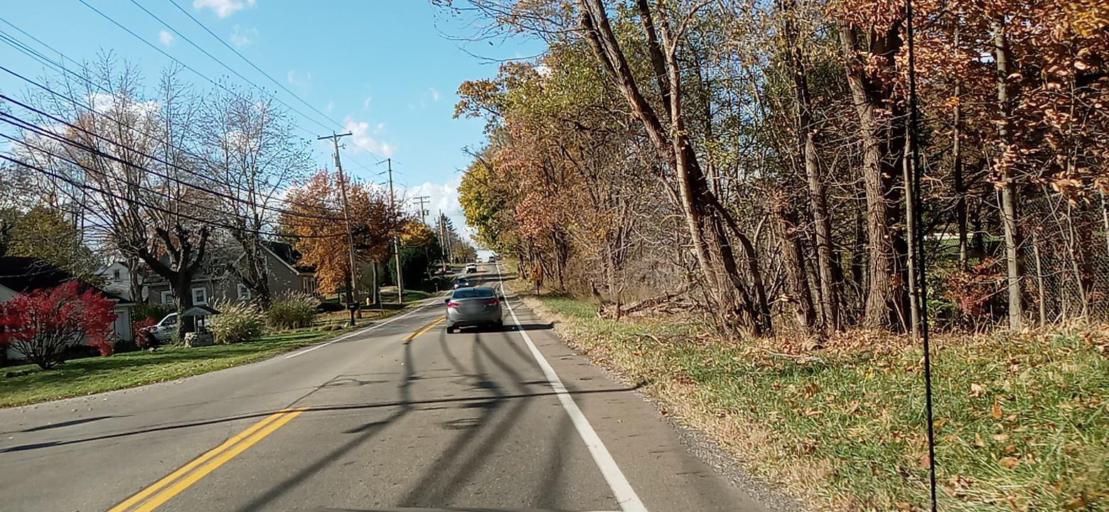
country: US
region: Ohio
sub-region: Summit County
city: Portage Lakes
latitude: 40.9979
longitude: -81.5104
